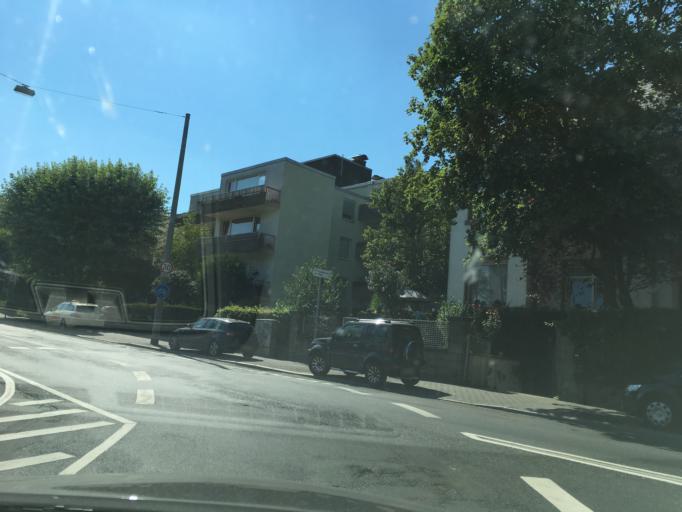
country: DE
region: Hesse
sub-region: Regierungsbezirk Darmstadt
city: Frankfurt am Main
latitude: 50.1391
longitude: 8.7172
